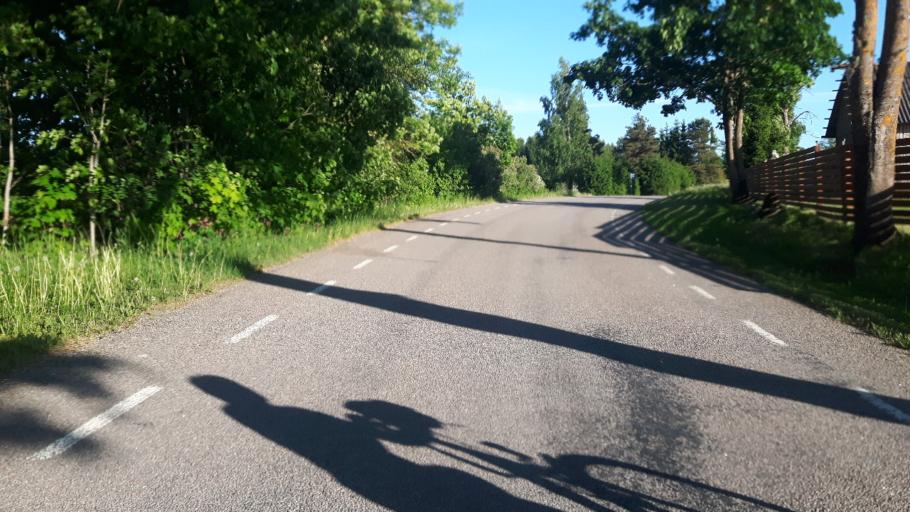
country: EE
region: Raplamaa
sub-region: Kehtna vald
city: Kehtna
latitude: 58.8987
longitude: 24.8795
